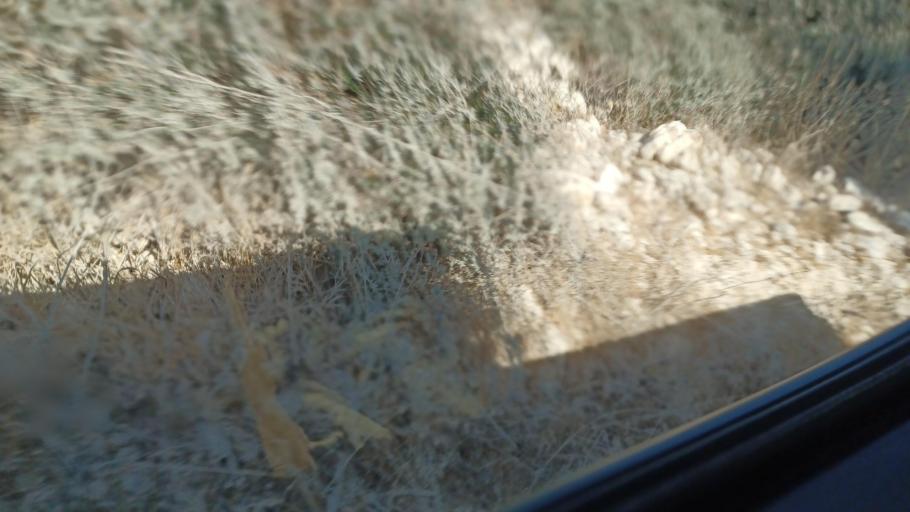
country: CY
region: Pafos
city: Tala
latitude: 34.8663
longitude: 32.4584
